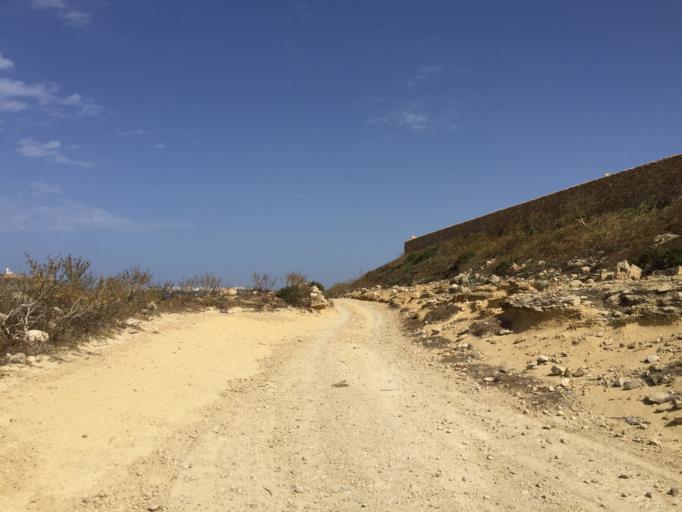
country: MT
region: L-Gharb
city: Gharb
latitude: 36.0720
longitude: 14.2009
